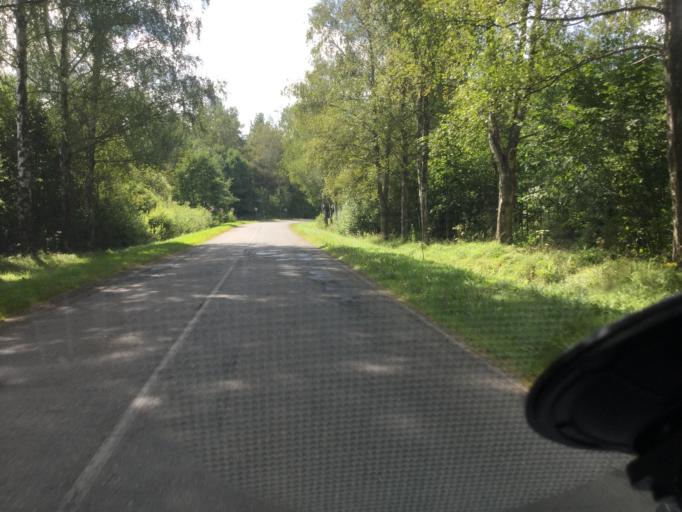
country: BY
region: Vitebsk
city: Chashniki
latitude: 55.3013
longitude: 29.3909
